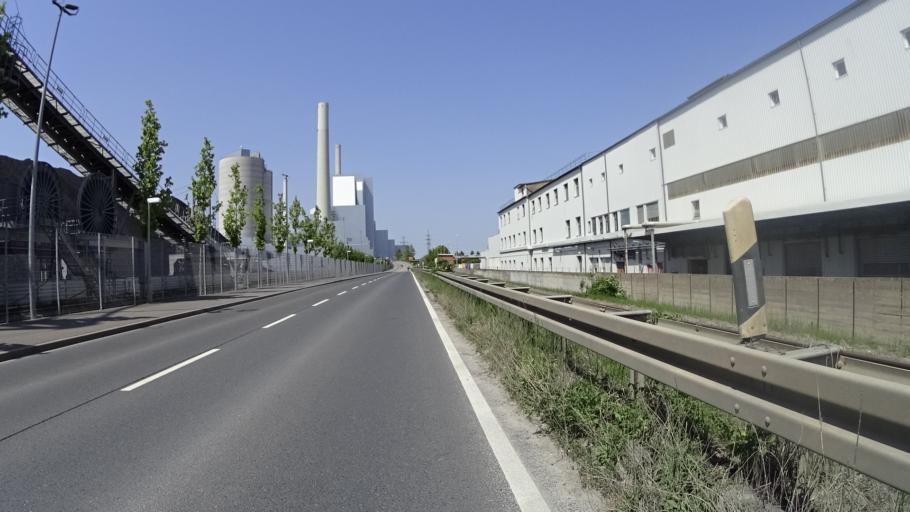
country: DE
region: Rheinland-Pfalz
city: Altrip
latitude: 49.4390
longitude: 8.5124
